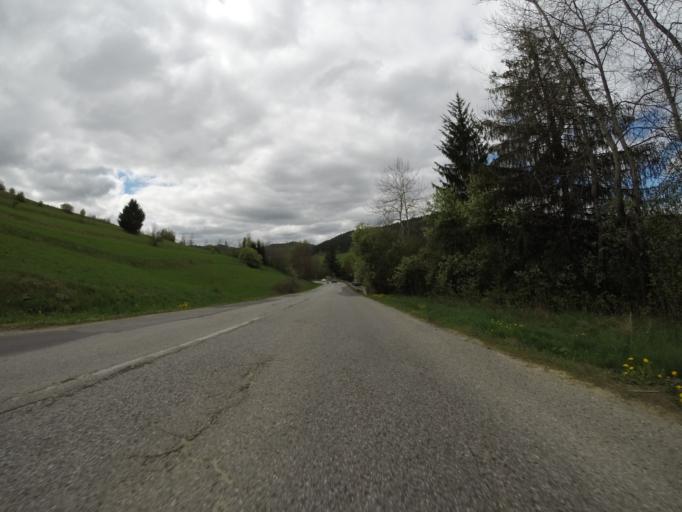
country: SK
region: Banskobystricky
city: Cierny Balog
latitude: 48.7624
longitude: 19.6294
